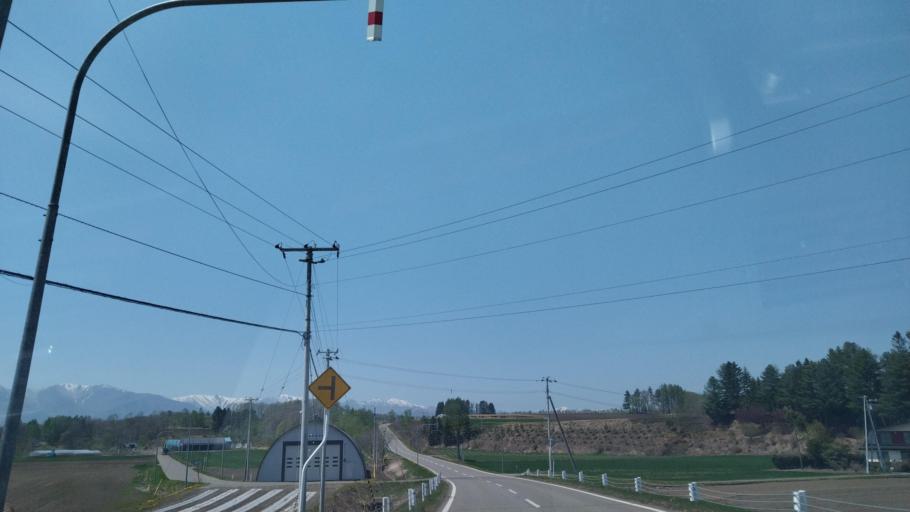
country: JP
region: Hokkaido
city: Obihiro
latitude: 42.9029
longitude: 143.0098
